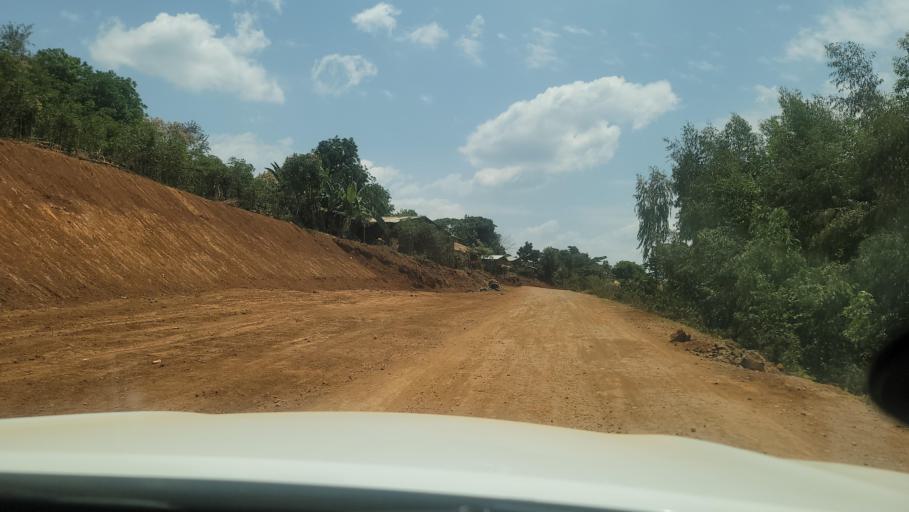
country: ET
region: Oromiya
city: Agaro
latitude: 7.8043
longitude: 36.4592
